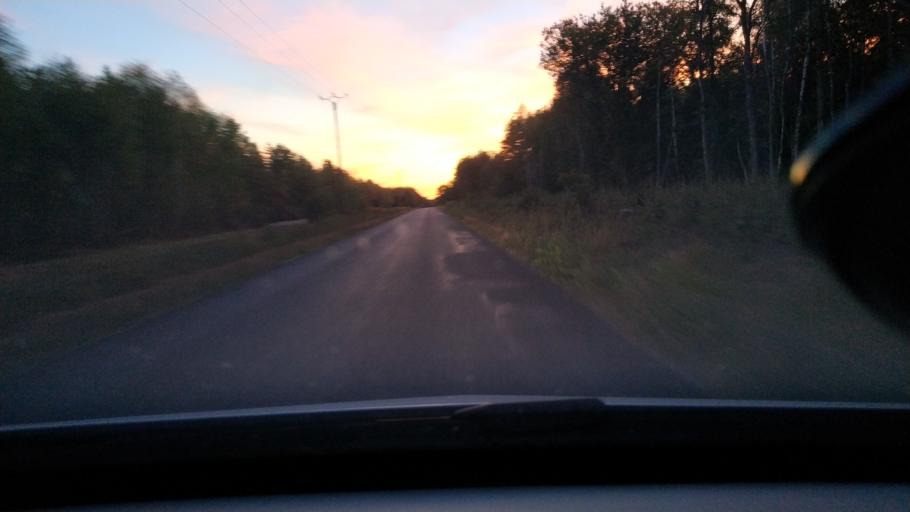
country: FR
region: Centre
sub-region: Departement du Cher
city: Brinon-sur-Sauldre
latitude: 47.6172
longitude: 2.2104
